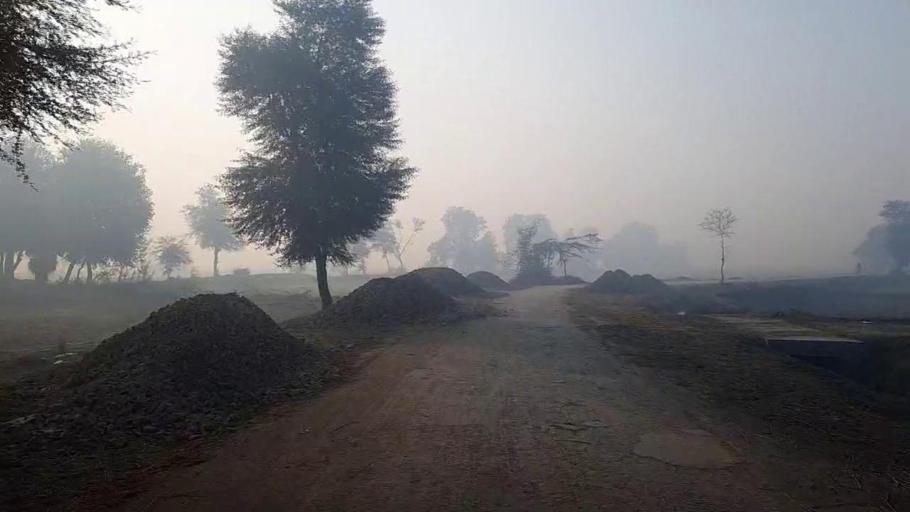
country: PK
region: Sindh
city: Mehar
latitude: 27.1634
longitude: 67.8249
